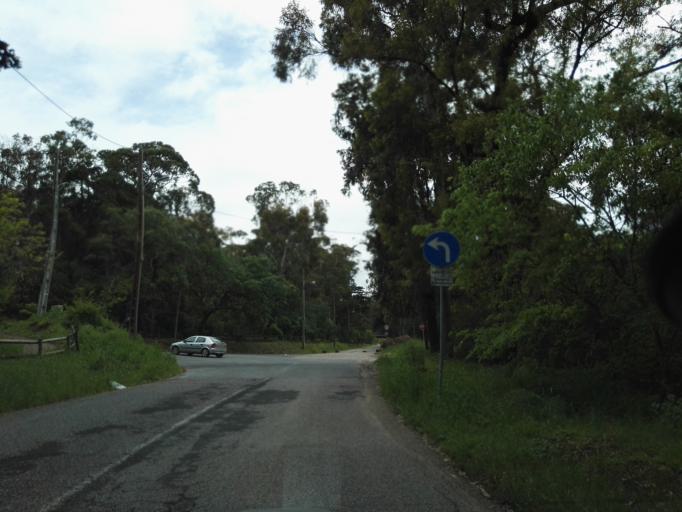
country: PT
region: Lisbon
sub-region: Oeiras
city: Alges
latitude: 38.7261
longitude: -9.1995
